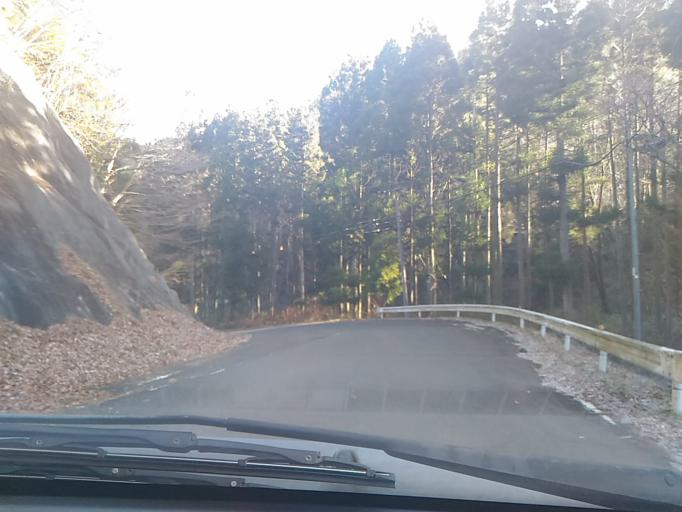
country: JP
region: Fukushima
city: Ishikawa
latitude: 36.9979
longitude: 140.5438
